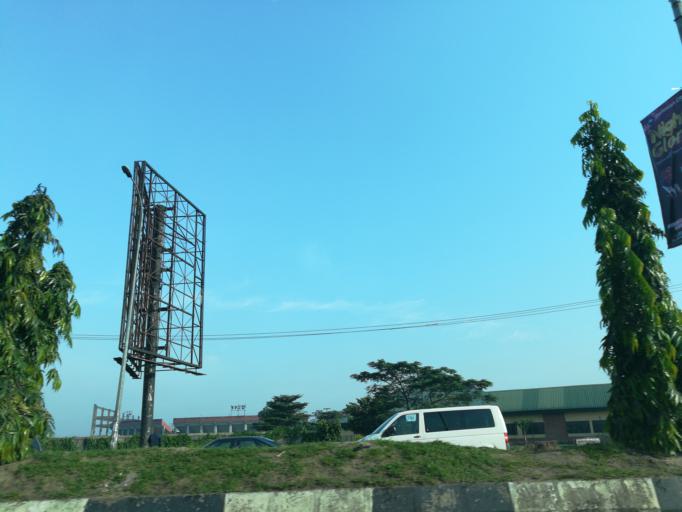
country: NG
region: Rivers
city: Port Harcourt
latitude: 4.8223
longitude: 7.0223
